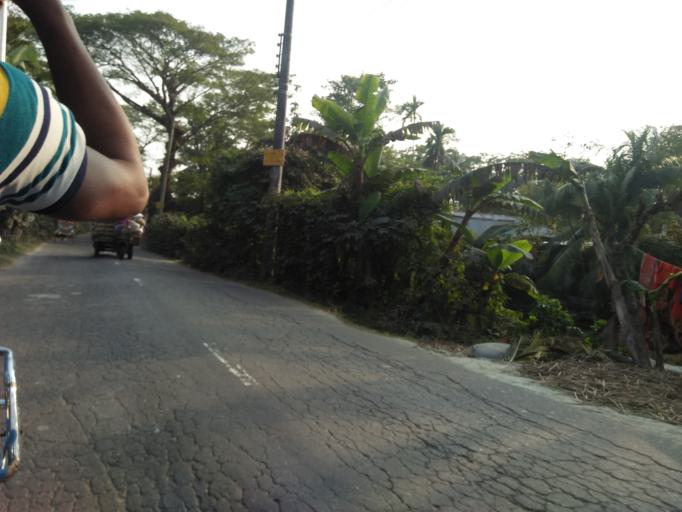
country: BD
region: Barisal
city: Bhola
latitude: 22.6988
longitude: 90.6427
